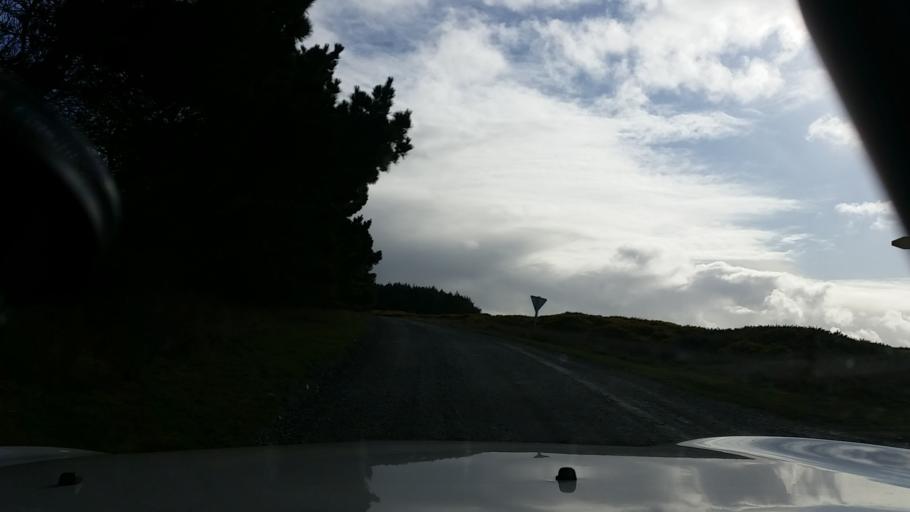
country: NZ
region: Chatham Islands
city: Waitangi
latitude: -43.8327
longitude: -176.5403
